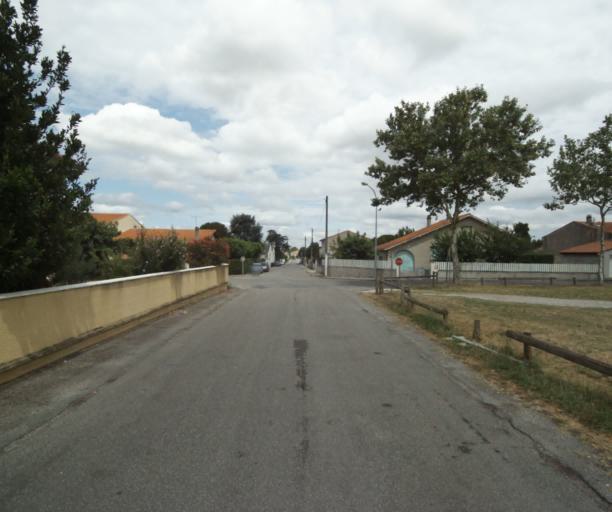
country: FR
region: Midi-Pyrenees
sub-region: Departement de la Haute-Garonne
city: Revel
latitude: 43.4544
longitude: 1.9994
